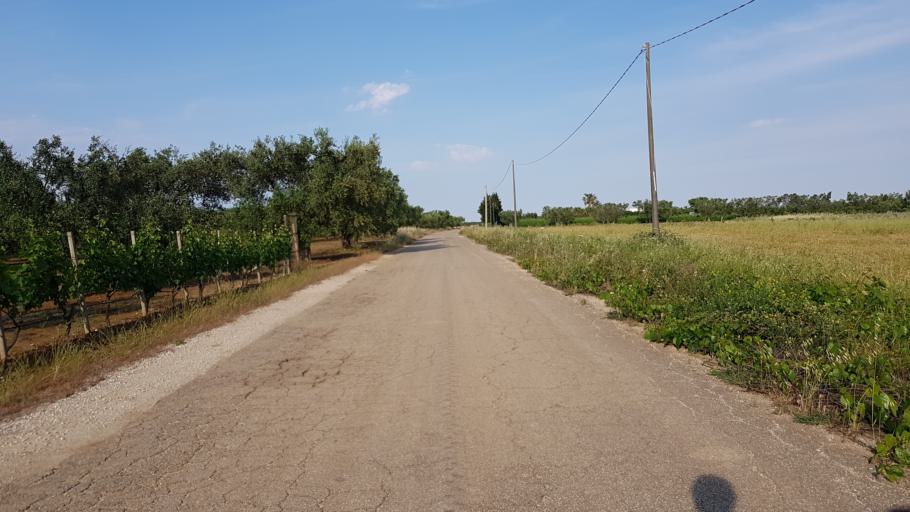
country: IT
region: Apulia
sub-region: Provincia di Brindisi
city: Mesagne
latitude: 40.6206
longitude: 17.7908
